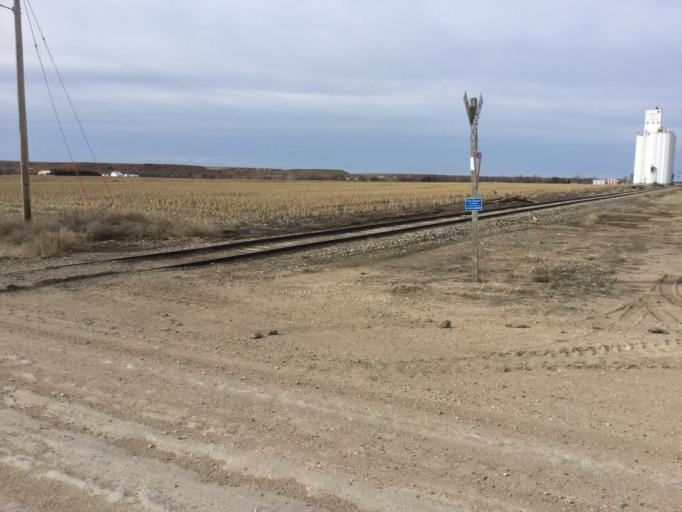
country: US
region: Kansas
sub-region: Lane County
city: Dighton
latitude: 38.4602
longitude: -100.3020
